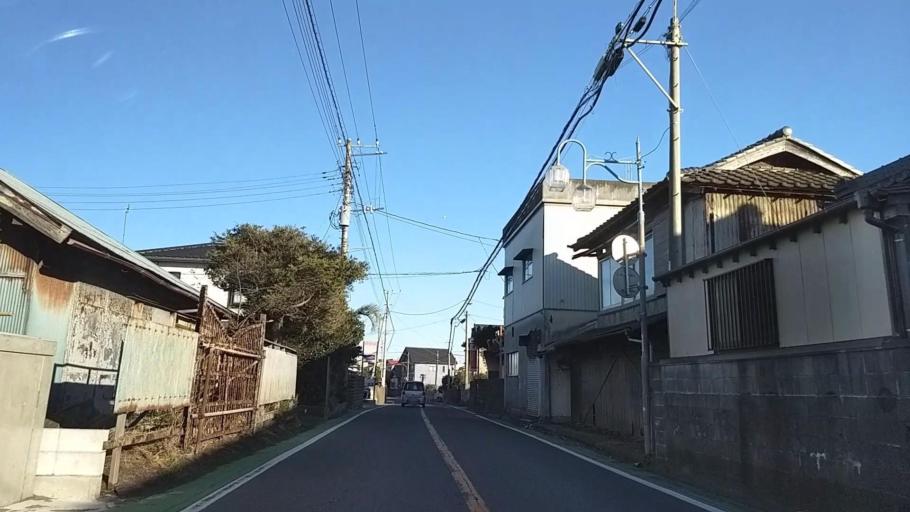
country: JP
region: Chiba
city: Asahi
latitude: 35.6942
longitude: 140.6643
